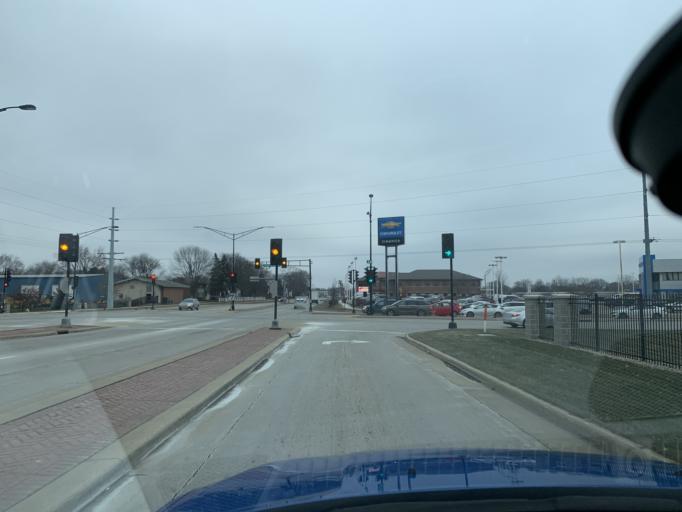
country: US
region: Wisconsin
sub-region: Dane County
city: Sun Prairie
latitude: 43.1765
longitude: -89.2456
